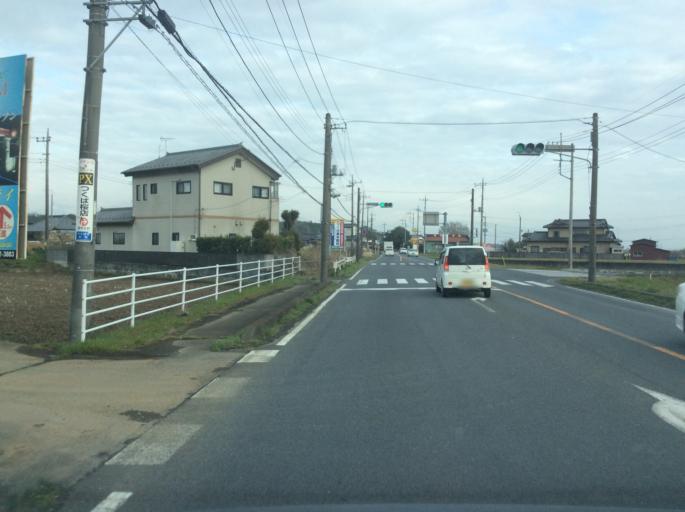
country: JP
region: Ibaraki
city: Tsukuba
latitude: 36.1360
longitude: 140.1336
